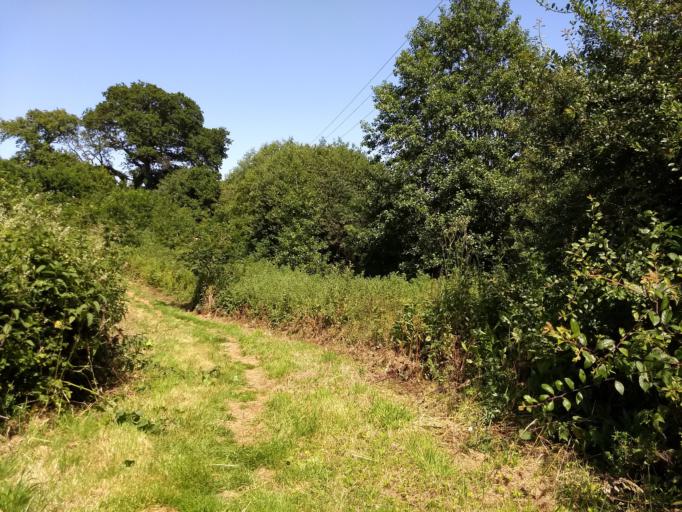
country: GB
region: England
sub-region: Isle of Wight
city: Shalfleet
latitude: 50.6885
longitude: -1.4164
